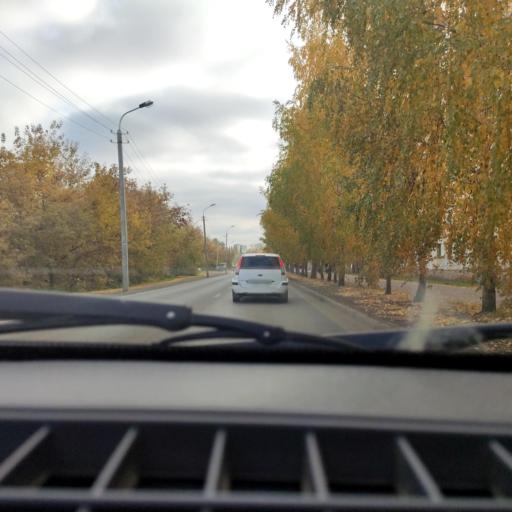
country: RU
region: Bashkortostan
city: Mikhaylovka
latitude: 54.7082
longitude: 55.8393
